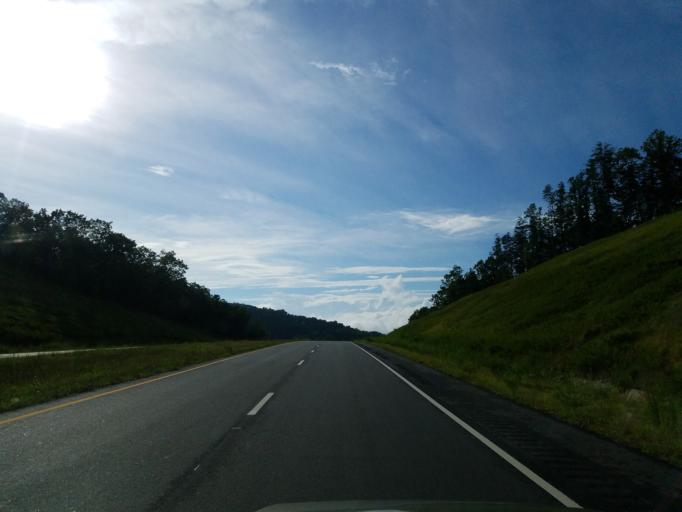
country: US
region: Georgia
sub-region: White County
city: Cleveland
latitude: 34.5811
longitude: -83.7676
